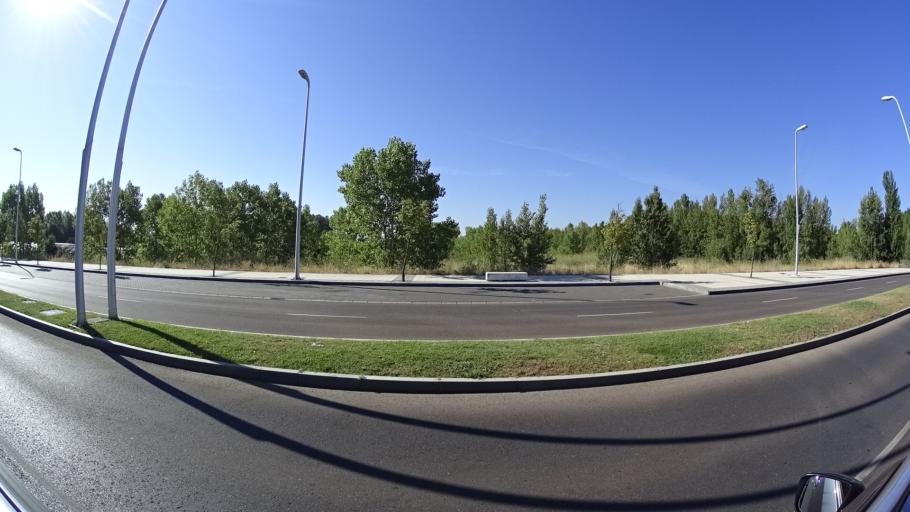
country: ES
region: Castille and Leon
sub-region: Provincia de Leon
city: Leon
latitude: 42.5807
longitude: -5.5698
